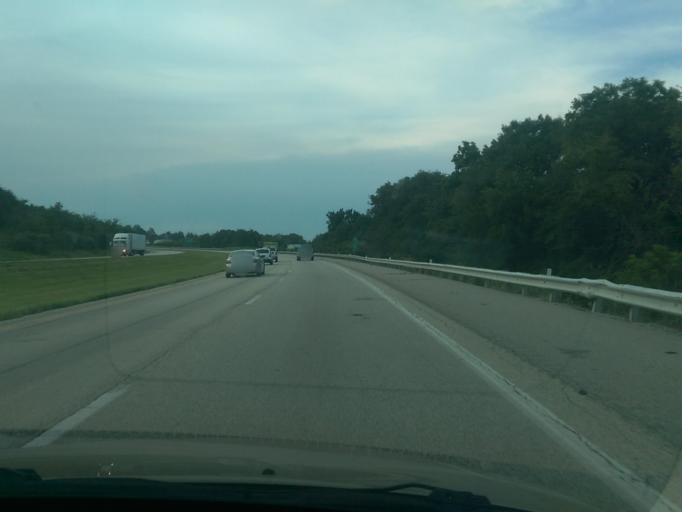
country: US
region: Missouri
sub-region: Andrew County
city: Country Club Village
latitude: 39.8510
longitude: -94.8051
